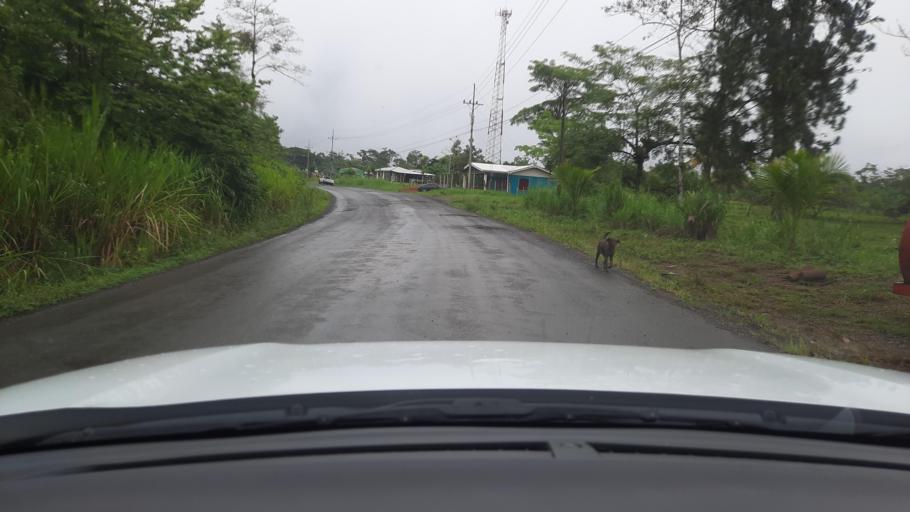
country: CR
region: Alajuela
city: San Jose
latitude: 11.0099
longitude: -85.3483
